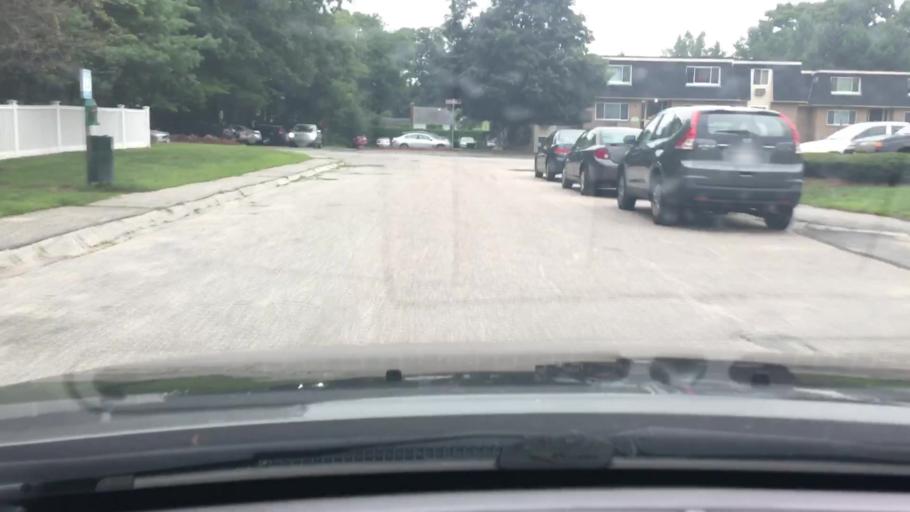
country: US
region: Massachusetts
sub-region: Worcester County
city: Hopedale
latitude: 42.1570
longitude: -71.5371
